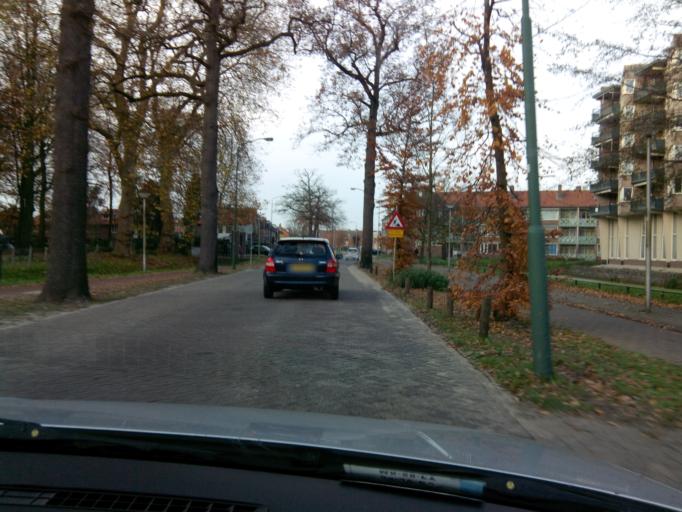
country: NL
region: Utrecht
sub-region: Gemeente Amersfoort
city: Randenbroek
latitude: 52.1503
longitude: 5.4007
